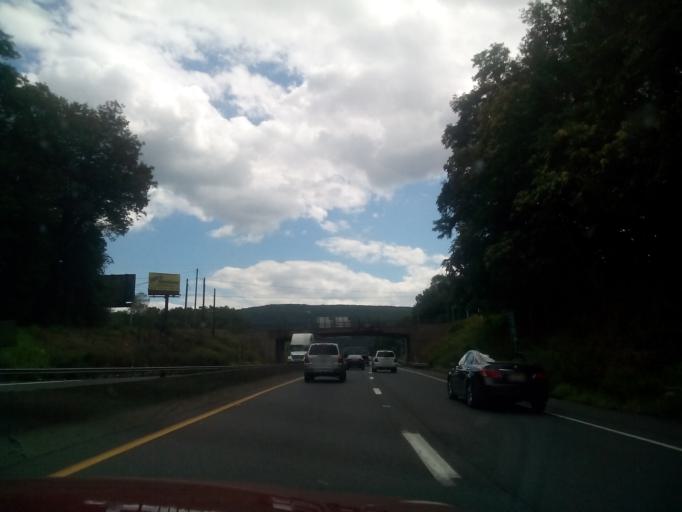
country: US
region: Pennsylvania
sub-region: Monroe County
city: East Stroudsburg
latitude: 40.9861
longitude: -75.1386
